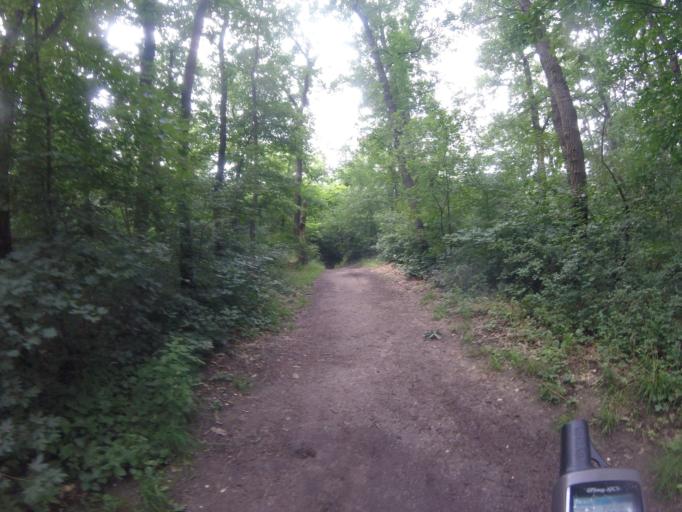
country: HU
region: Pest
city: Toeroekbalint
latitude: 47.4229
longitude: 18.9148
